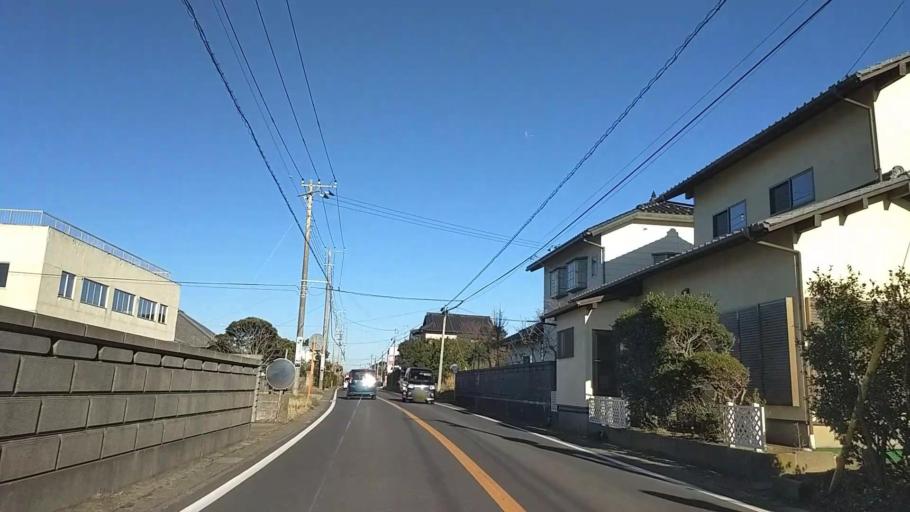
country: JP
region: Chiba
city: Yokaichiba
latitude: 35.6470
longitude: 140.5811
